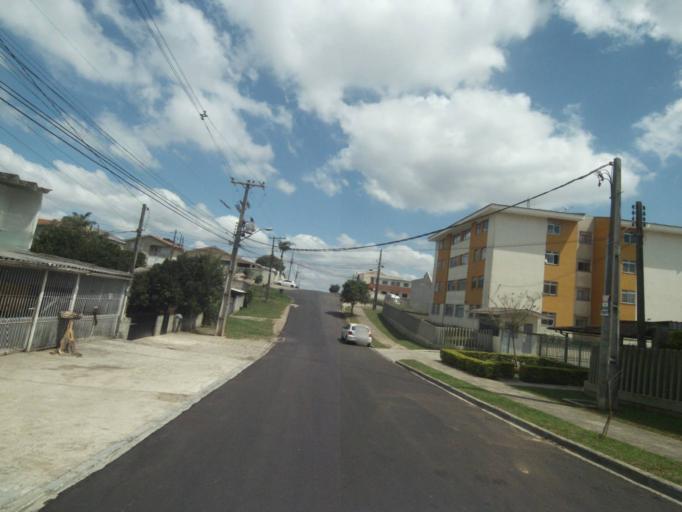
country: BR
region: Parana
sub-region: Curitiba
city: Curitiba
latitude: -25.5029
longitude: -49.3064
